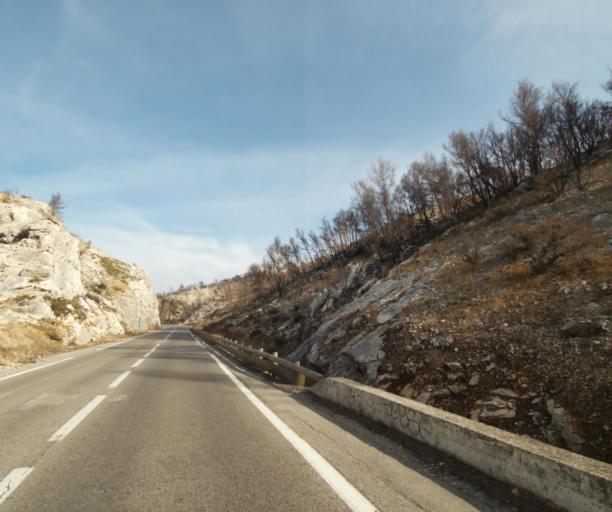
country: FR
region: Provence-Alpes-Cote d'Azur
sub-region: Departement des Bouches-du-Rhone
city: Carry-le-Rouet
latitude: 43.3394
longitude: 5.1791
